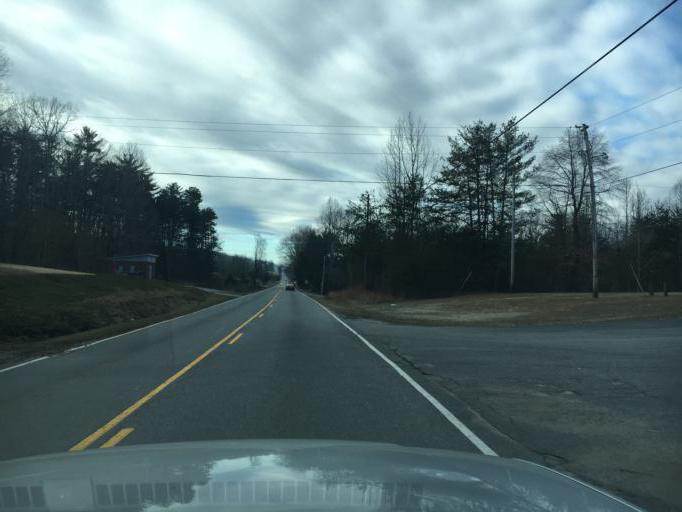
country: US
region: North Carolina
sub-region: Burke County
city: Salem
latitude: 35.6900
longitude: -81.7238
